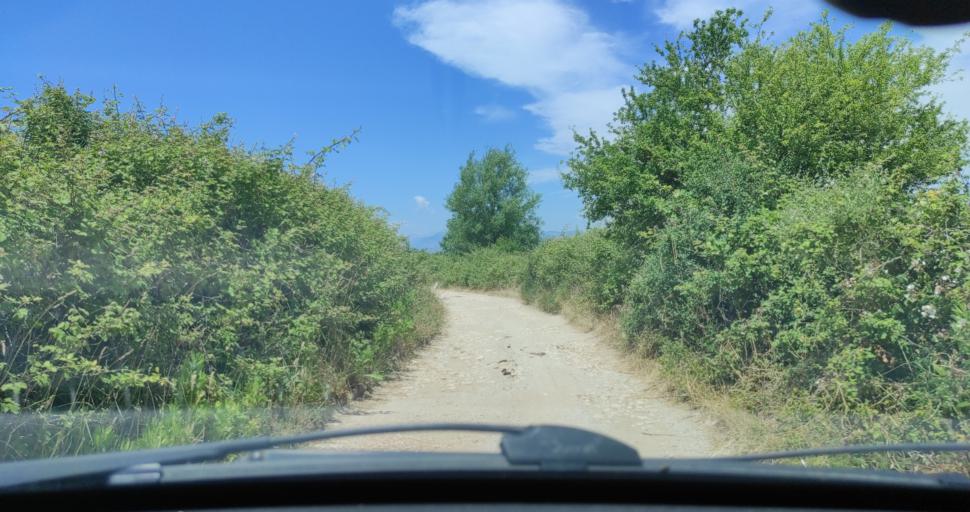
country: AL
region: Shkoder
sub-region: Rrethi i Shkodres
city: Velipoje
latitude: 41.8819
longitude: 19.3928
